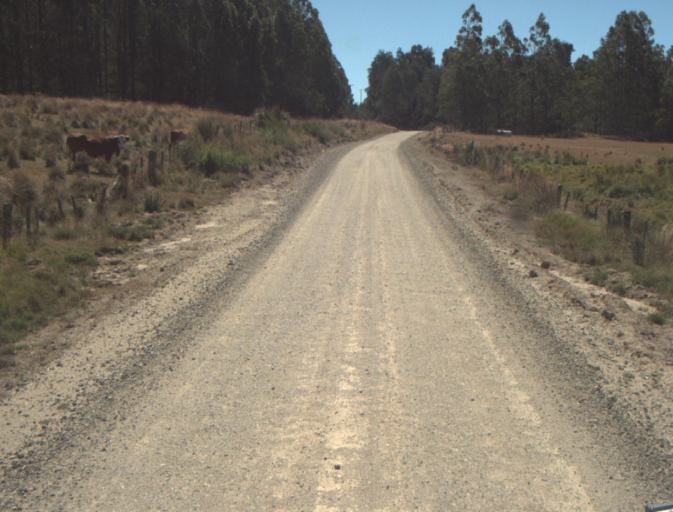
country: AU
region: Tasmania
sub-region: Dorset
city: Scottsdale
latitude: -41.3667
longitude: 147.4679
